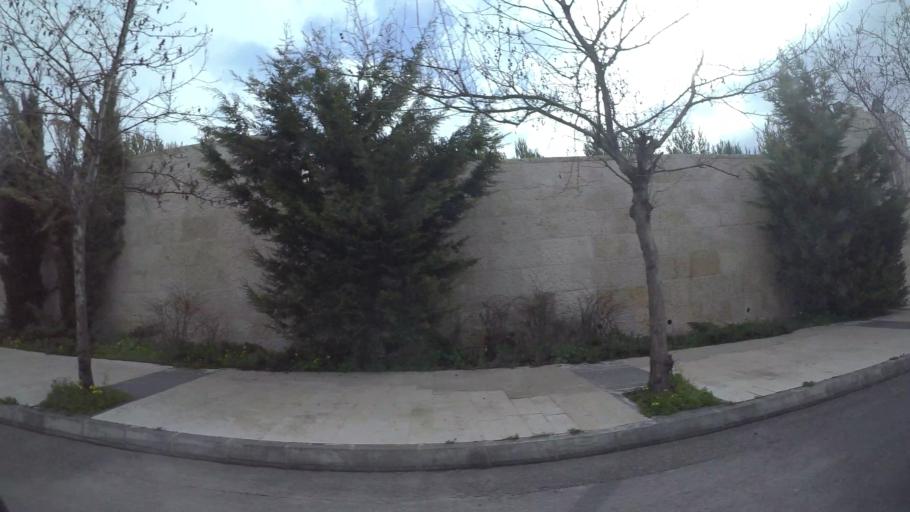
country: JO
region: Amman
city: Wadi as Sir
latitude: 31.9842
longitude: 35.8210
